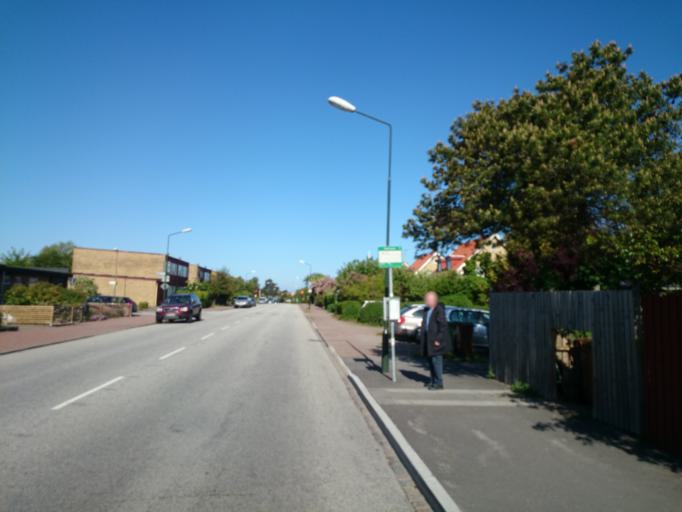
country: SE
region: Skane
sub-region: Malmo
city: Malmoe
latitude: 55.5785
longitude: 12.9635
